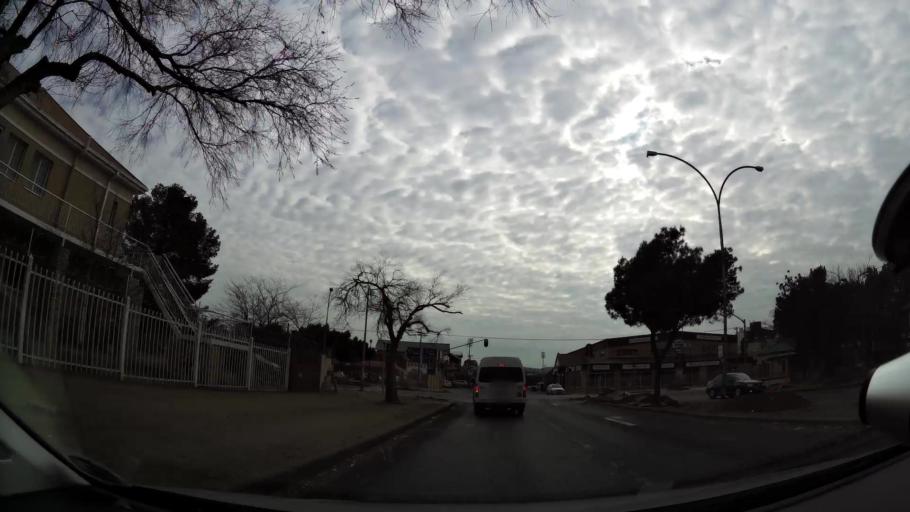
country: ZA
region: Orange Free State
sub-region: Mangaung Metropolitan Municipality
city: Bloemfontein
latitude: -29.1225
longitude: 26.2034
